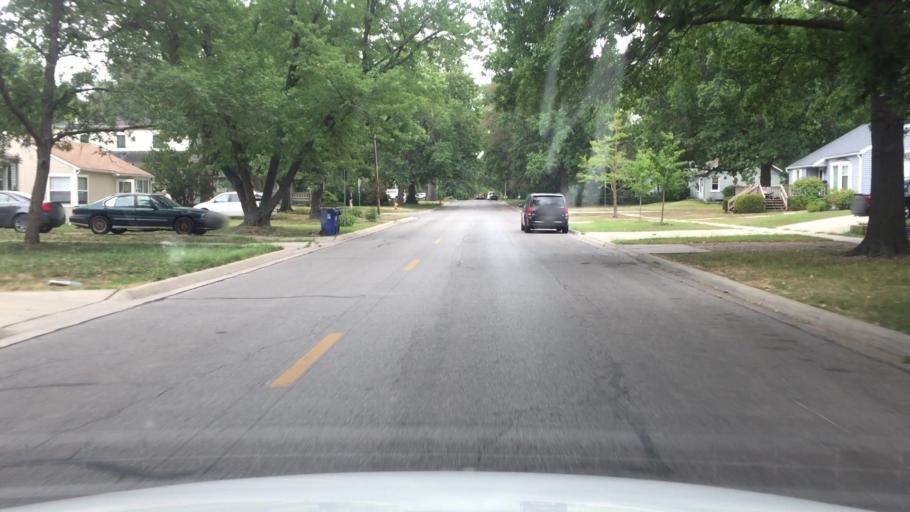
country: US
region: Kansas
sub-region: Douglas County
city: Lawrence
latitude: 38.9455
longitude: -95.2394
